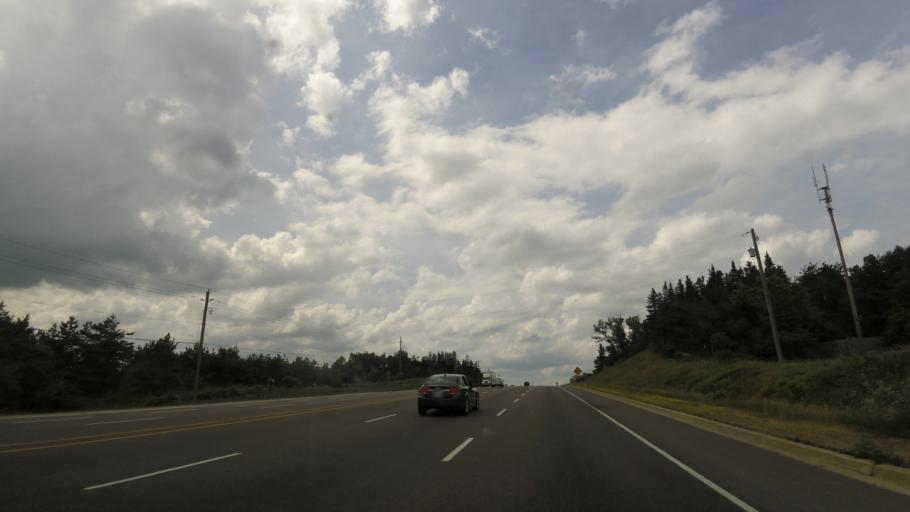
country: CA
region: Ontario
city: Orangeville
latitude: 43.8433
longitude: -79.9728
